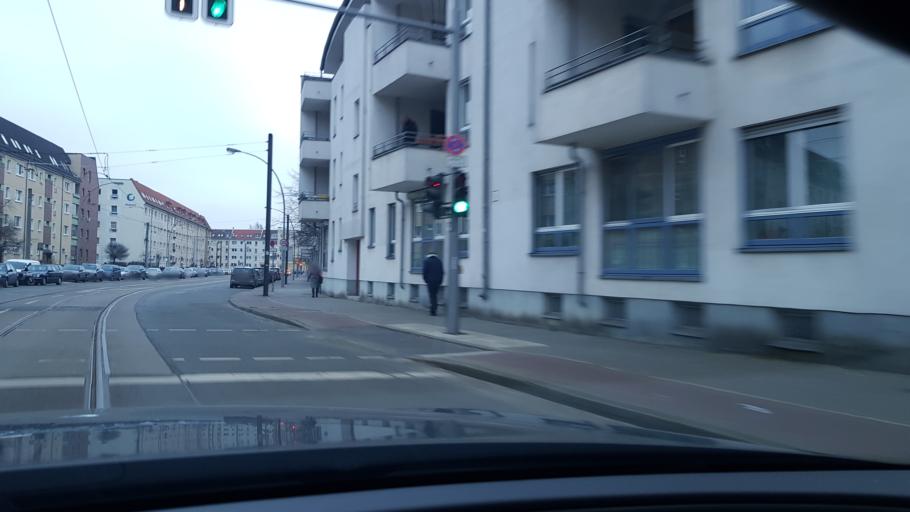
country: DE
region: Berlin
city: Berlin Koepenick
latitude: 52.4403
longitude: 13.5817
